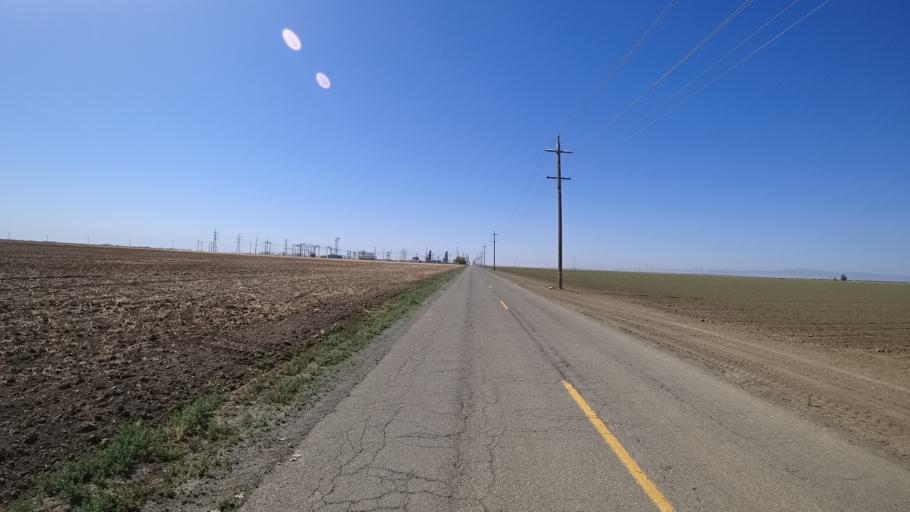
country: US
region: California
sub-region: Kings County
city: Lemoore Station
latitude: 36.2467
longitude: -119.9052
